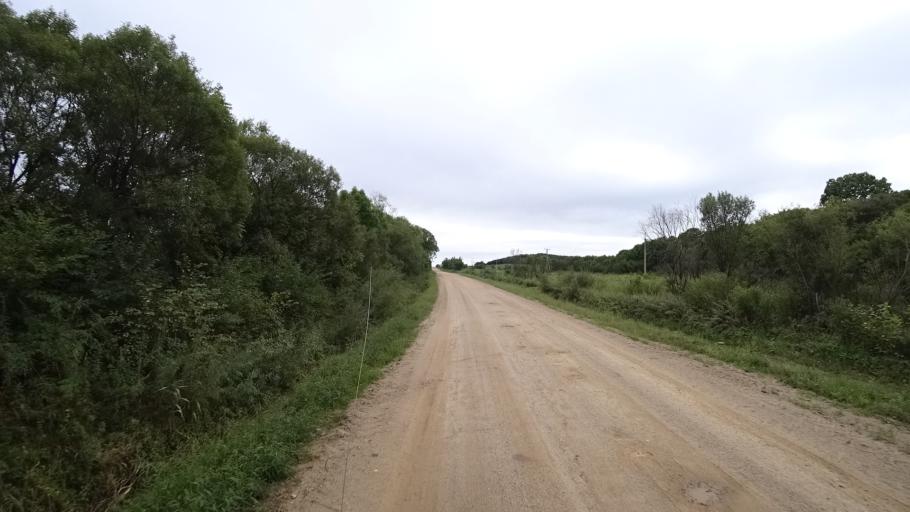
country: RU
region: Primorskiy
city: Monastyrishche
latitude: 44.0985
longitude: 132.6025
